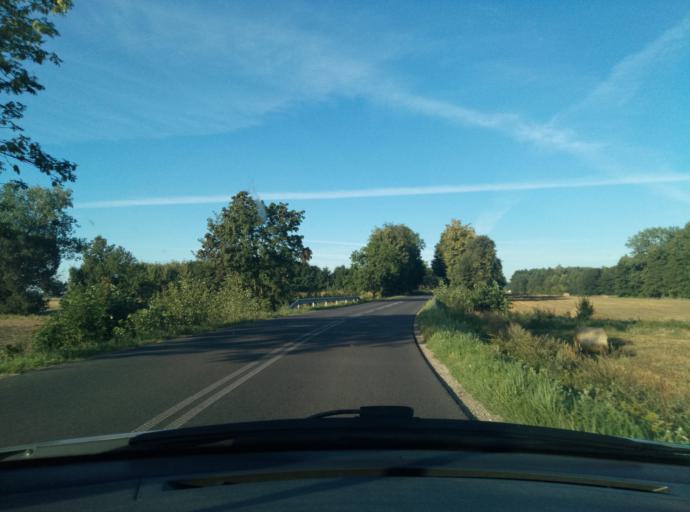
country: PL
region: Kujawsko-Pomorskie
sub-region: Powiat wabrzeski
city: Wabrzezno
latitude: 53.2253
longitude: 18.9524
